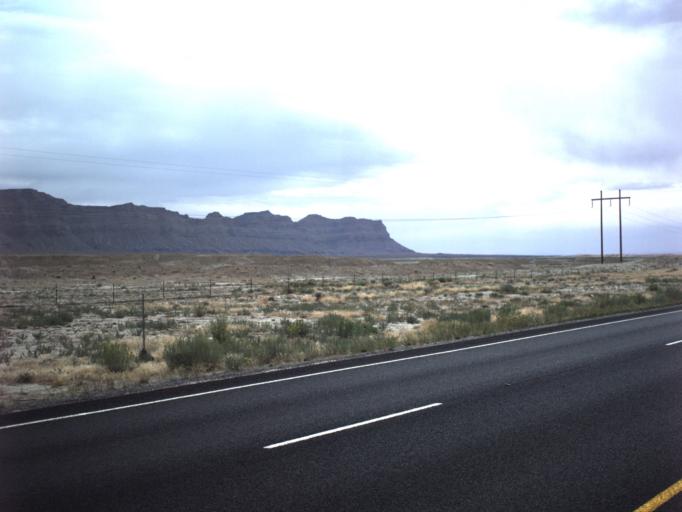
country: US
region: Utah
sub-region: Carbon County
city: East Carbon City
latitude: 39.1704
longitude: -110.3383
